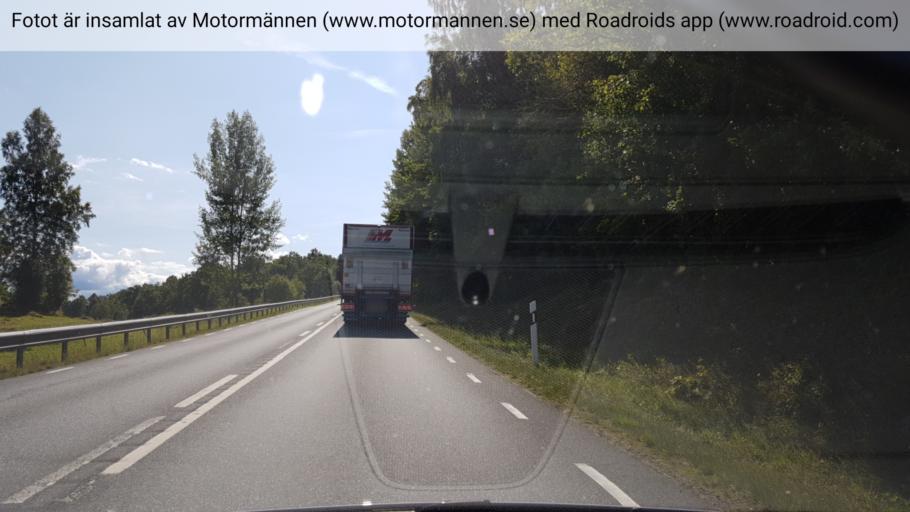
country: SE
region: Joenkoeping
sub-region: Jonkopings Kommun
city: Graenna
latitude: 58.0088
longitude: 14.5179
